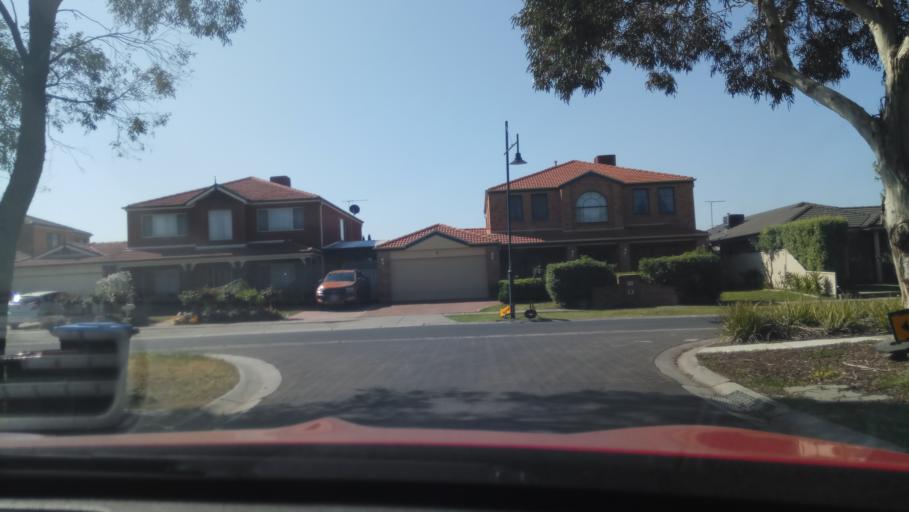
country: AU
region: Victoria
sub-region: Wyndham
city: Williams Landing
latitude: -37.8789
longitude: 144.7506
